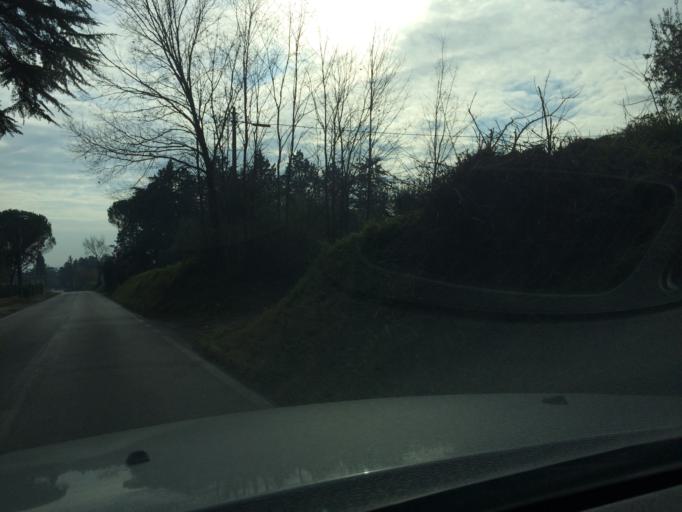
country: IT
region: Umbria
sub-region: Provincia di Perugia
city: Via Lippia
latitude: 43.0989
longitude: 12.4906
